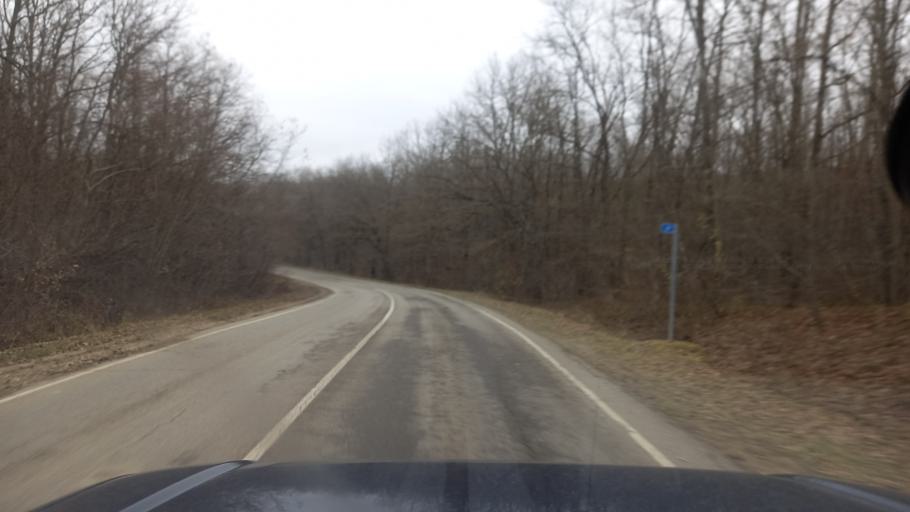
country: RU
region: Krasnodarskiy
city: Goryachiy Klyuch
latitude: 44.5439
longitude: 39.2673
